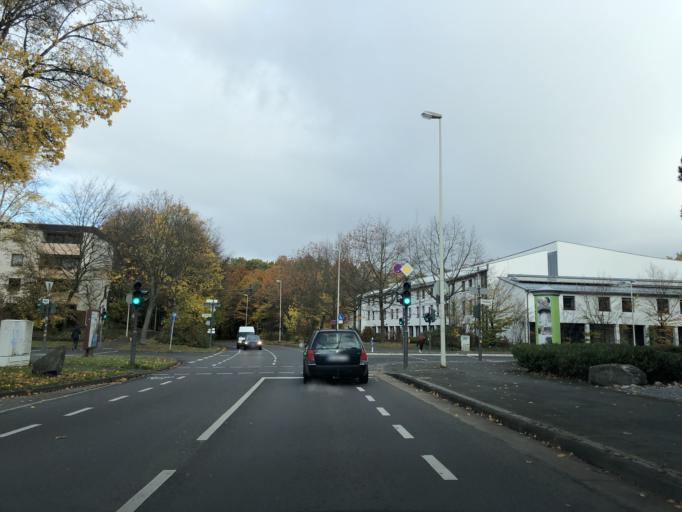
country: DE
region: North Rhine-Westphalia
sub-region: Regierungsbezirk Koln
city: Konigswinter
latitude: 50.6634
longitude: 7.1555
